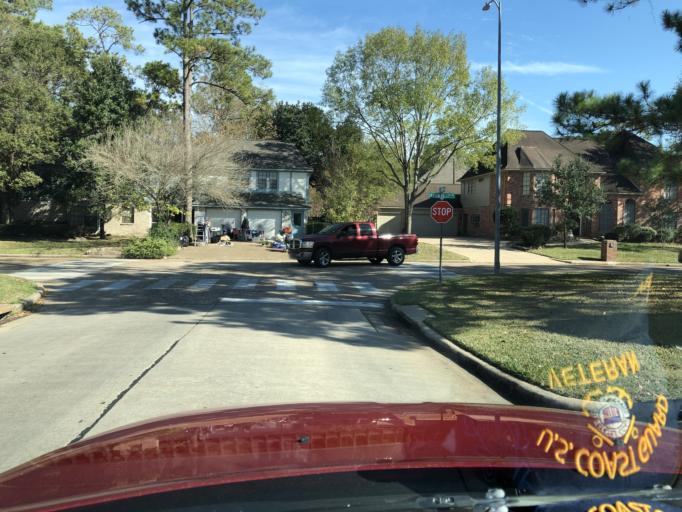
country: US
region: Texas
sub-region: Harris County
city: Tomball
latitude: 30.0211
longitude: -95.5502
